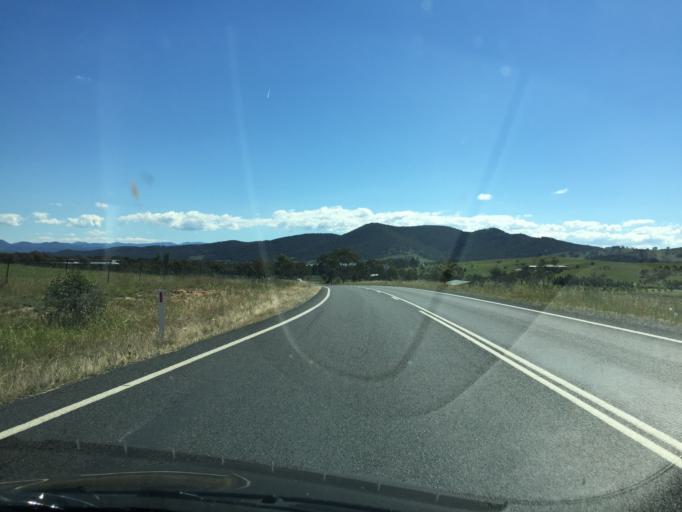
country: AU
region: Australian Capital Territory
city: Macarthur
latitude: -35.4785
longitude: 149.1686
